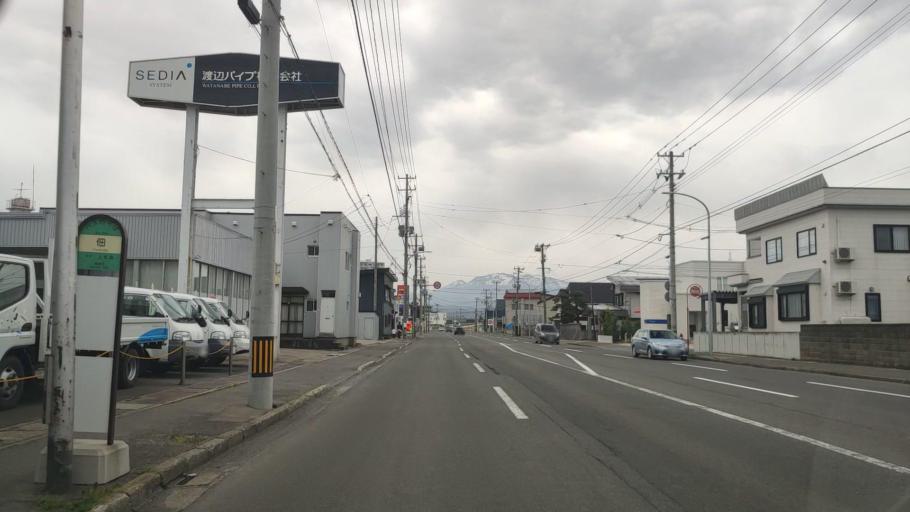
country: JP
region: Aomori
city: Aomori Shi
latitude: 40.8130
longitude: 140.7768
